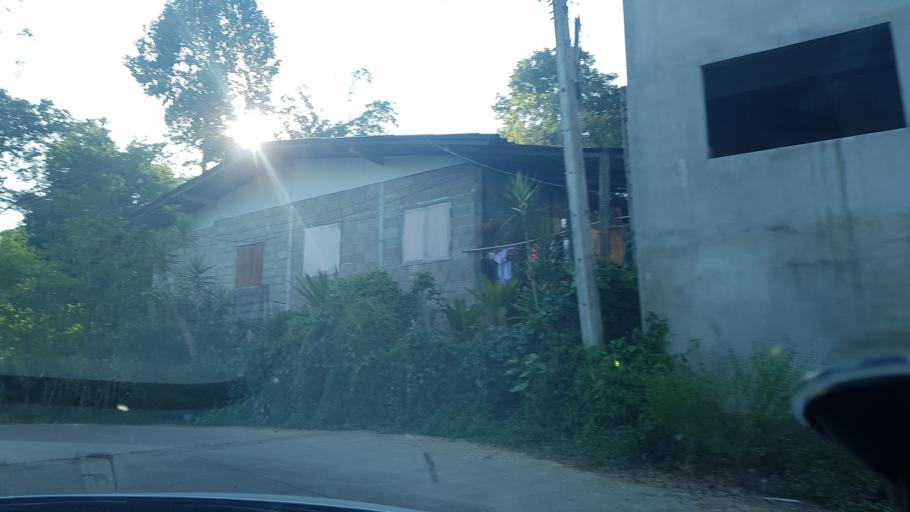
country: TH
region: Chiang Rai
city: Chiang Rai
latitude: 19.9475
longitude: 99.8070
